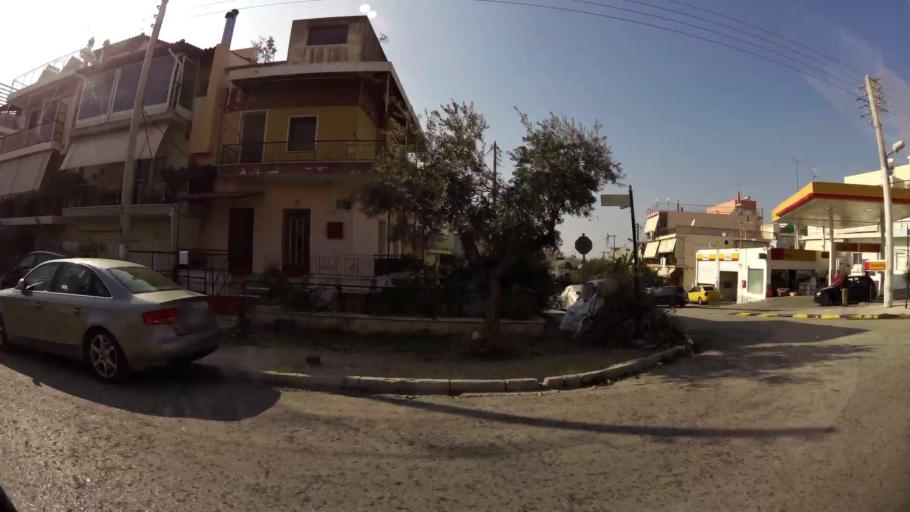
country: GR
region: Attica
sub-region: Nomarchia Athinas
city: Argyroupoli
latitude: 37.9191
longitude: 23.7506
